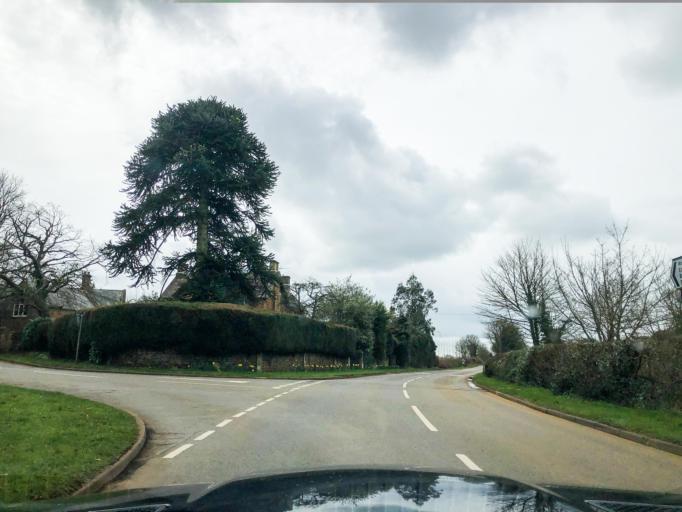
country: GB
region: England
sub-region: Oxfordshire
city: Hanwell
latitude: 52.1231
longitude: -1.4562
